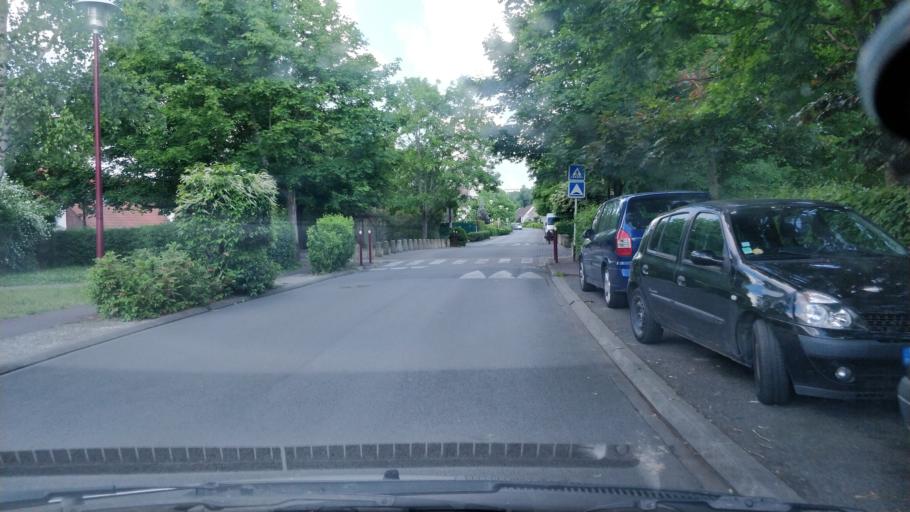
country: FR
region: Ile-de-France
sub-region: Departement de Seine-Saint-Denis
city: Bondy
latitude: 48.8902
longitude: 2.4814
